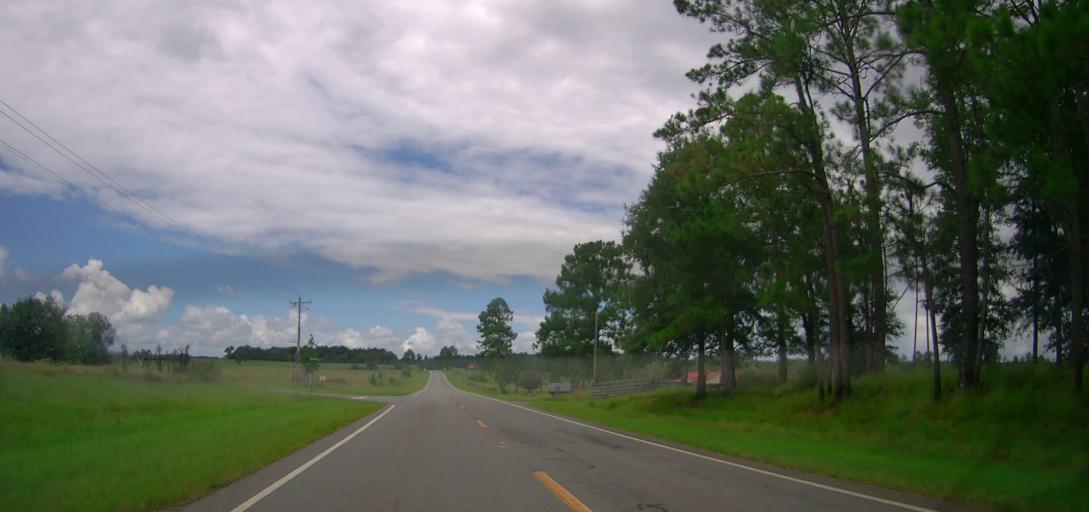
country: US
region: Georgia
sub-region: Wilcox County
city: Rochelle
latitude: 32.0272
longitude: -83.5666
